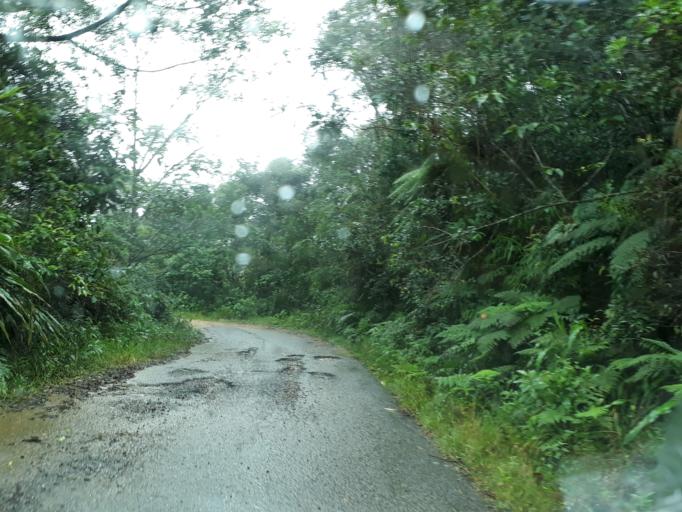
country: CO
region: Cundinamarca
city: Medina
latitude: 4.6658
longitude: -73.3265
